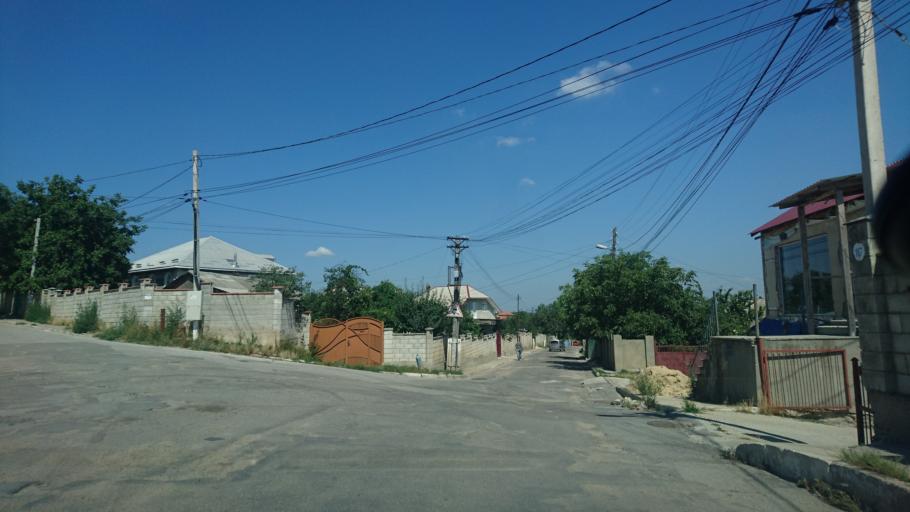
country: MD
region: Laloveni
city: Ialoveni
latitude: 47.0058
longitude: 28.7673
